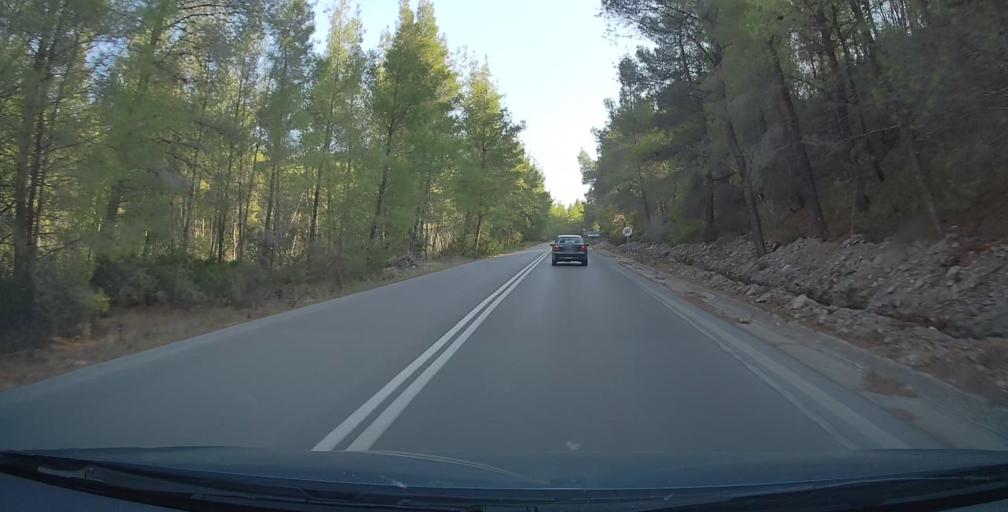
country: GR
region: Central Macedonia
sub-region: Nomos Chalkidikis
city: Neos Marmaras
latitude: 40.0757
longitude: 23.8061
